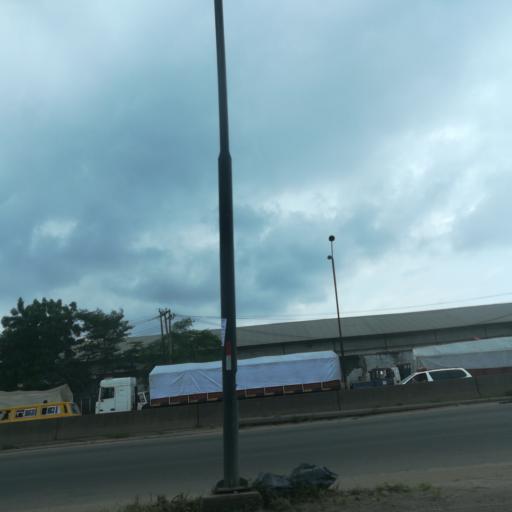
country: NG
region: Lagos
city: Mushin
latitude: 6.5337
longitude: 3.3363
